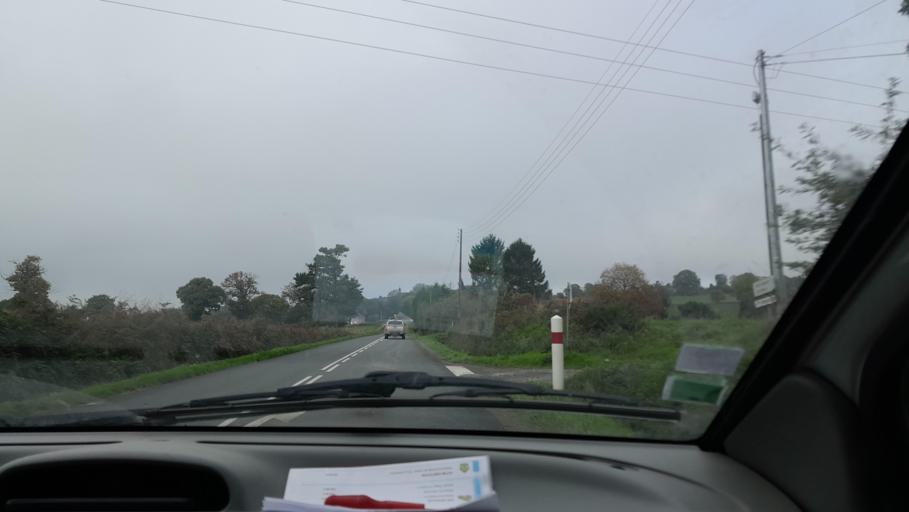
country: FR
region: Pays de la Loire
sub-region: Departement de la Mayenne
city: Juvigne
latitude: 48.2002
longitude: -1.0485
